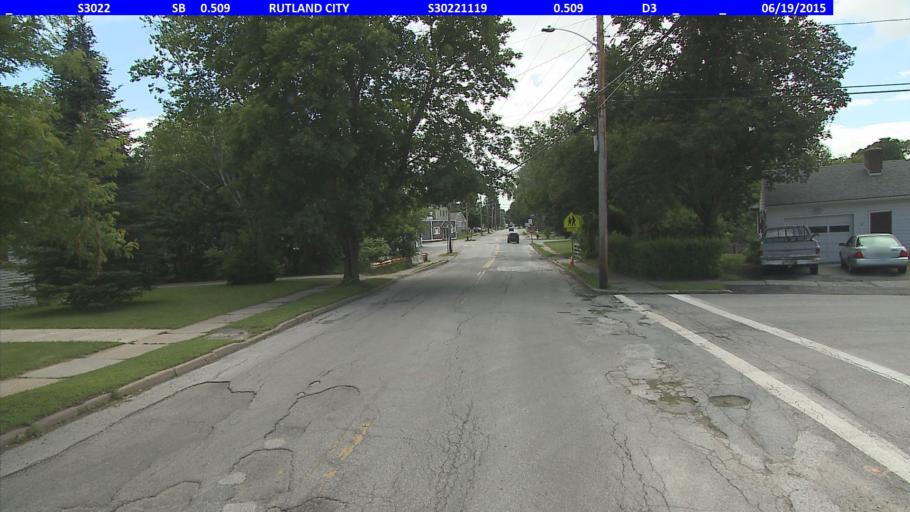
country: US
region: Vermont
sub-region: Rutland County
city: Rutland
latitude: 43.6161
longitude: -72.9840
